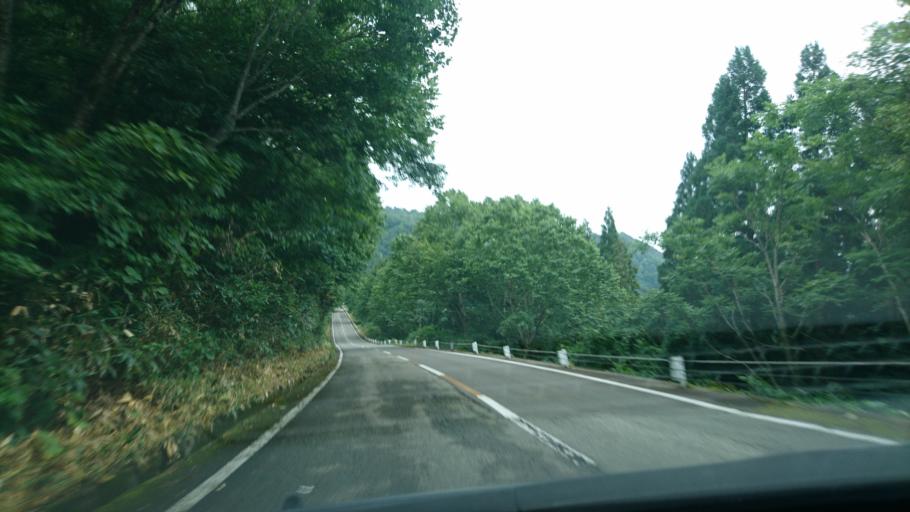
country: JP
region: Akita
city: Yuzawa
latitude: 38.9769
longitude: 140.7210
